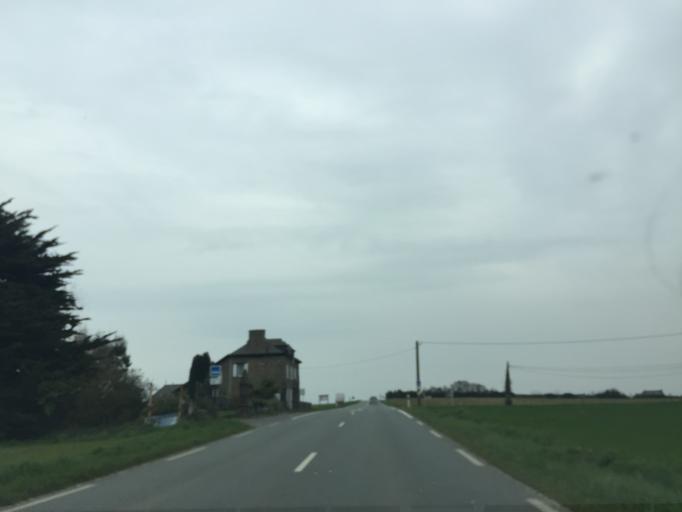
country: FR
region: Brittany
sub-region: Departement d'Ille-et-Vilaine
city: Saint-Coulomb
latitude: 48.6537
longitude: -1.9489
